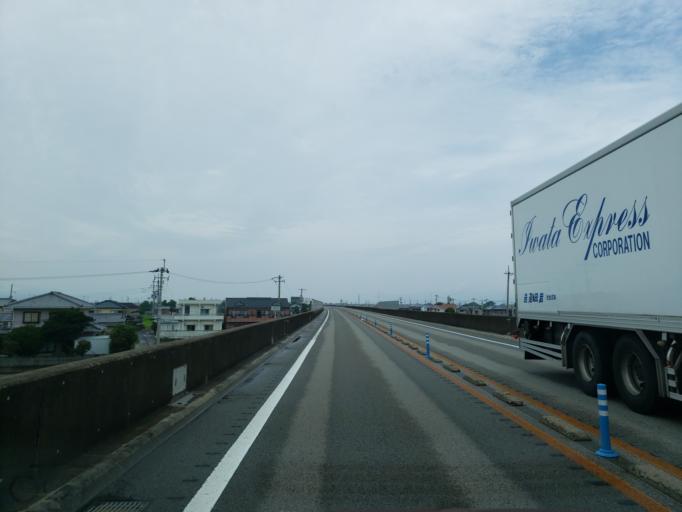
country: JP
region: Tokushima
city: Tokushima-shi
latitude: 34.1055
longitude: 134.5492
